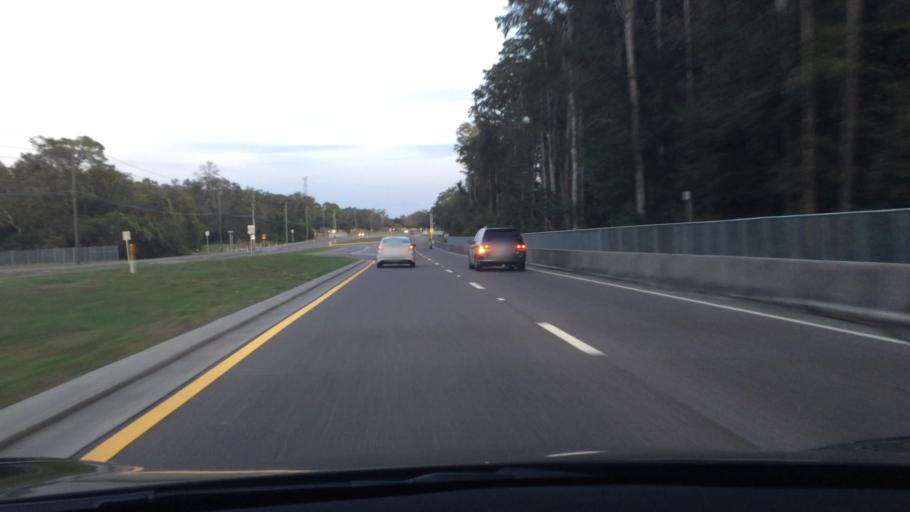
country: US
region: Florida
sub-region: Pasco County
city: Trinity
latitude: 28.1517
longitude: -82.7090
